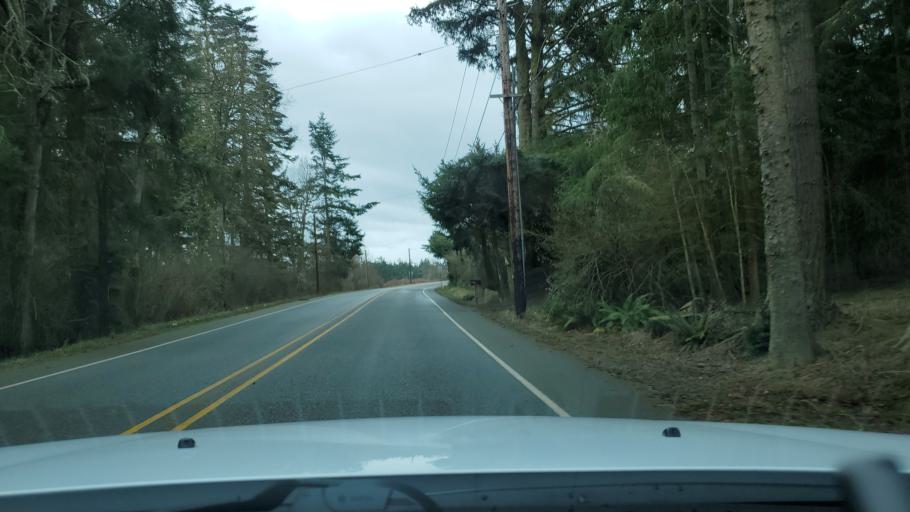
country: US
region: Washington
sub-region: Island County
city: Ault Field
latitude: 48.2876
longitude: -122.7261
